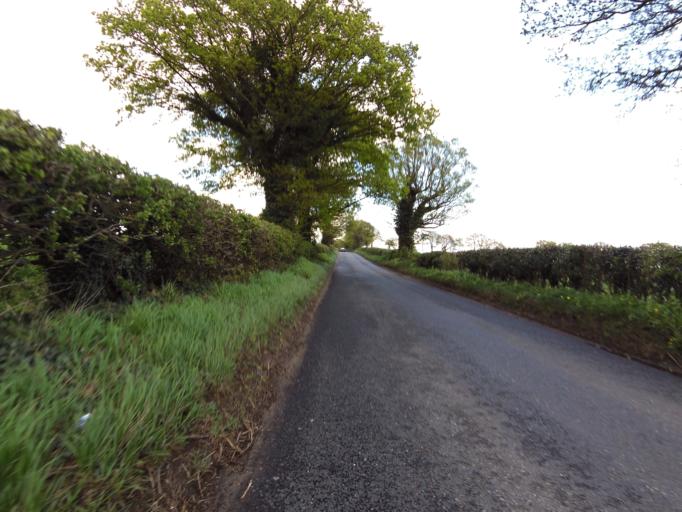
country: GB
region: England
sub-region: Suffolk
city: Kesgrave
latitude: 52.0704
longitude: 1.2226
